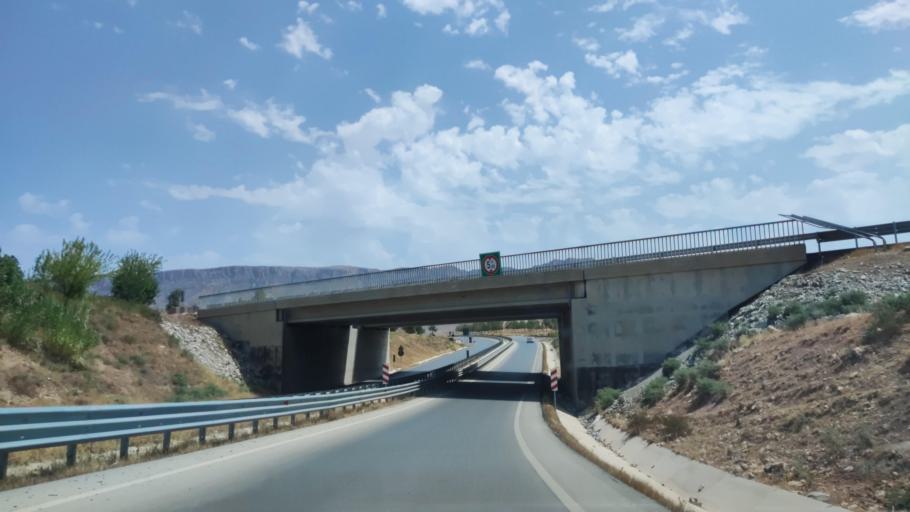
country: IQ
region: Arbil
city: Shaqlawah
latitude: 36.4570
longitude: 44.3836
